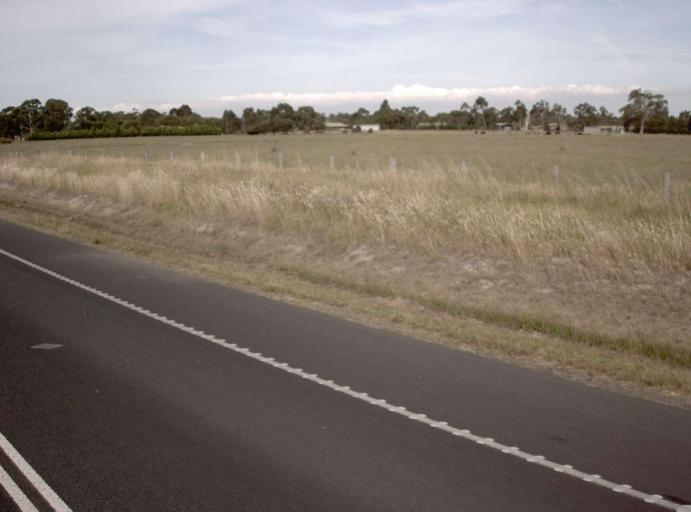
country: AU
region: Victoria
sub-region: Latrobe
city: Traralgon
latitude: -38.1314
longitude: 146.5597
